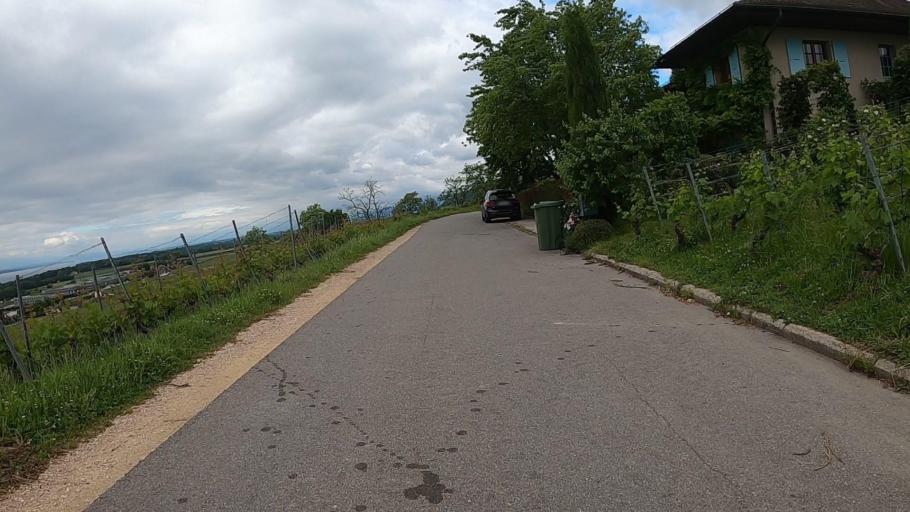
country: CH
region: Vaud
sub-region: Nyon District
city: Rolle
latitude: 46.4693
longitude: 6.3276
